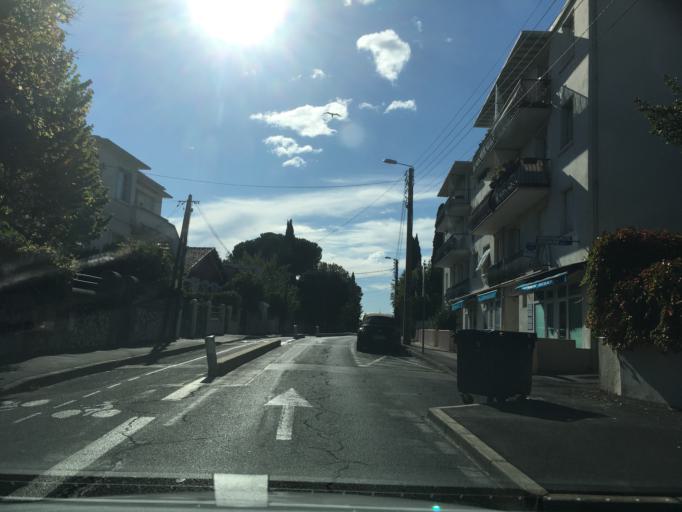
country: FR
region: Languedoc-Roussillon
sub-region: Departement de l'Herault
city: Montpellier
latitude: 43.5986
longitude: 3.8788
